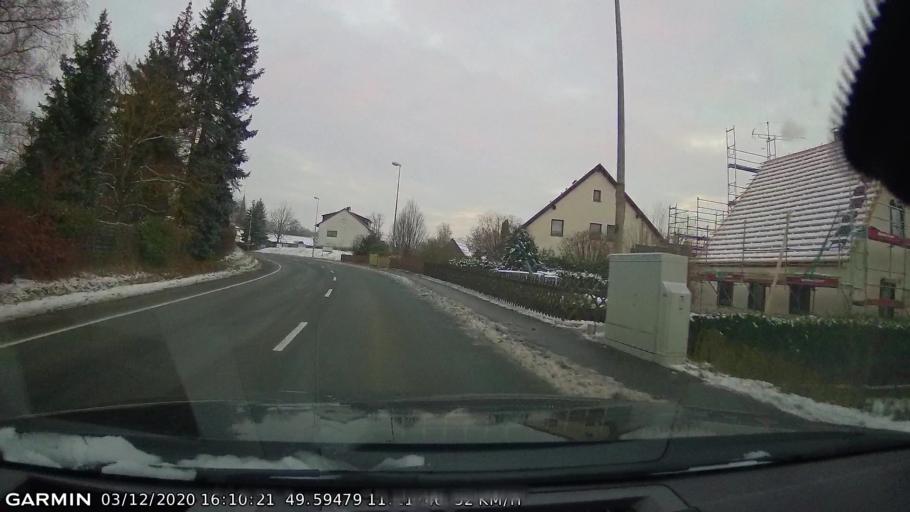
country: DE
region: Bavaria
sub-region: Upper Franconia
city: Dormitz
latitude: 49.5948
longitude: 11.1175
